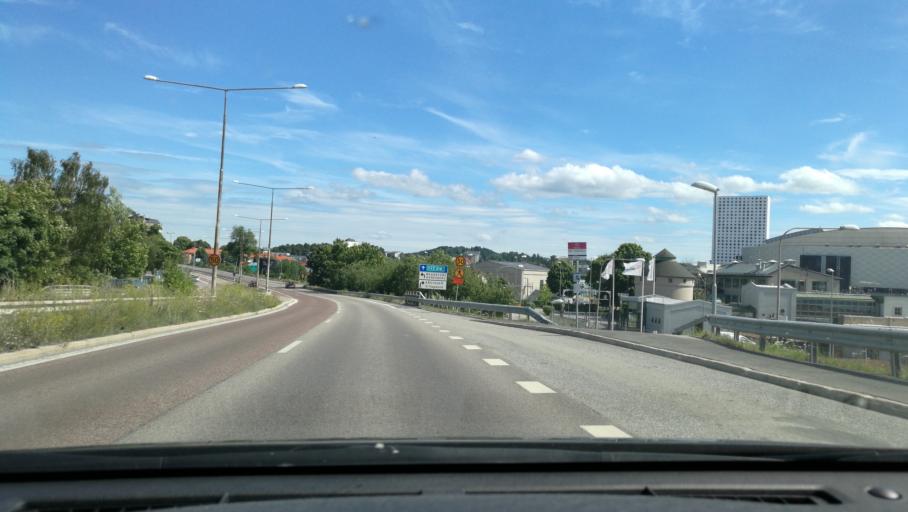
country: SE
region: Stockholm
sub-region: Solna Kommun
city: Rasunda
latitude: 59.3777
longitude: 17.9965
